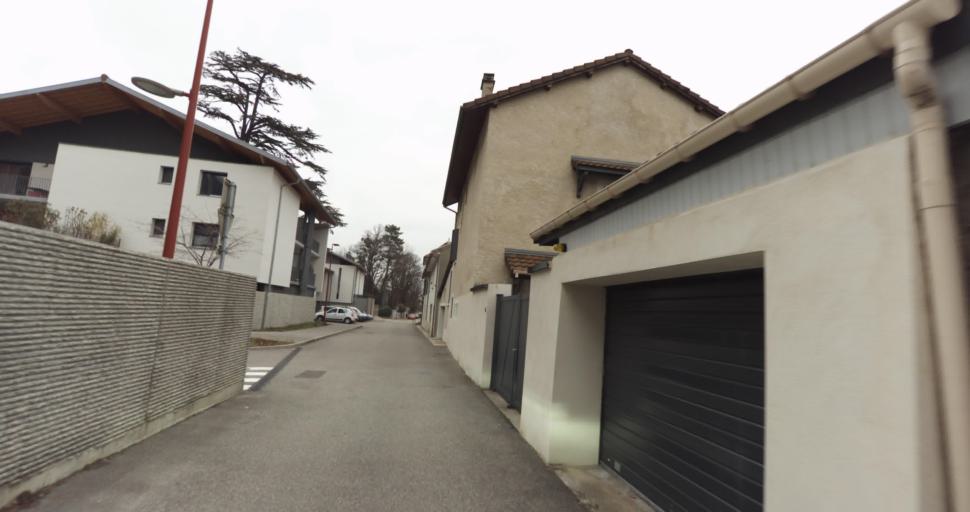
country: FR
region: Rhone-Alpes
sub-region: Departement de l'Isere
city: Vif
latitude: 45.0549
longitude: 5.6663
